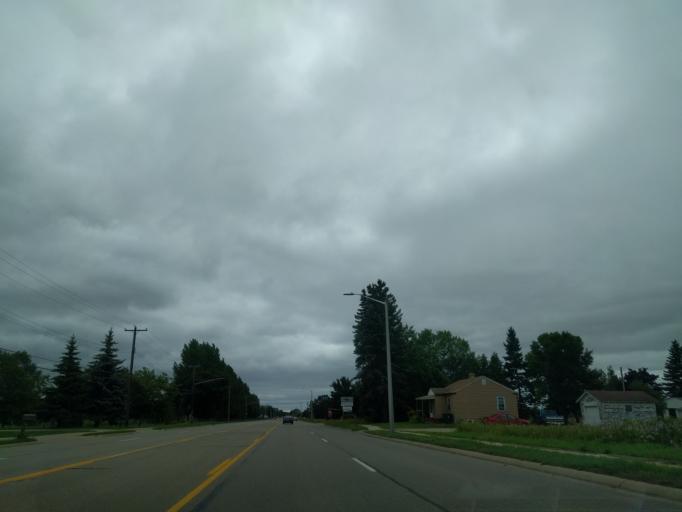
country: US
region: Michigan
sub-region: Delta County
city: Escanaba
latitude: 45.7310
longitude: -87.0799
